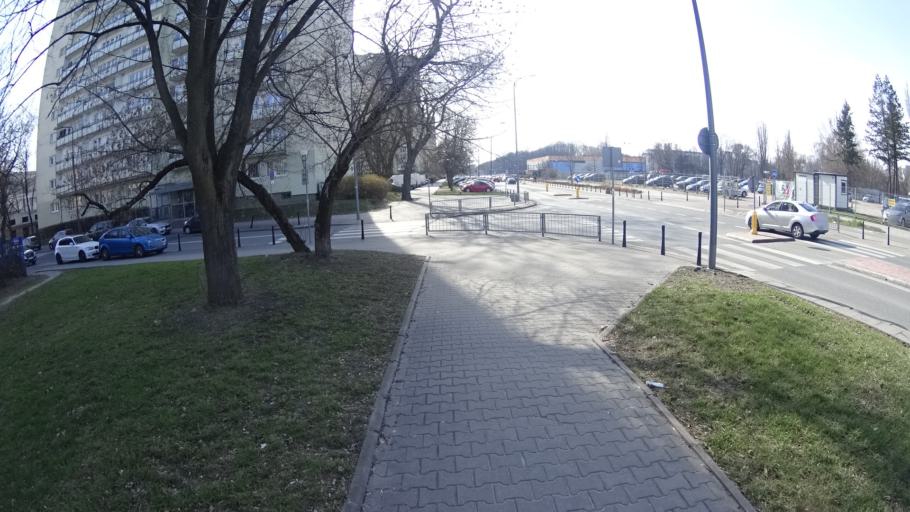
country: PL
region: Masovian Voivodeship
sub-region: Warszawa
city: Srodmiescie
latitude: 52.2115
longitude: 21.0132
